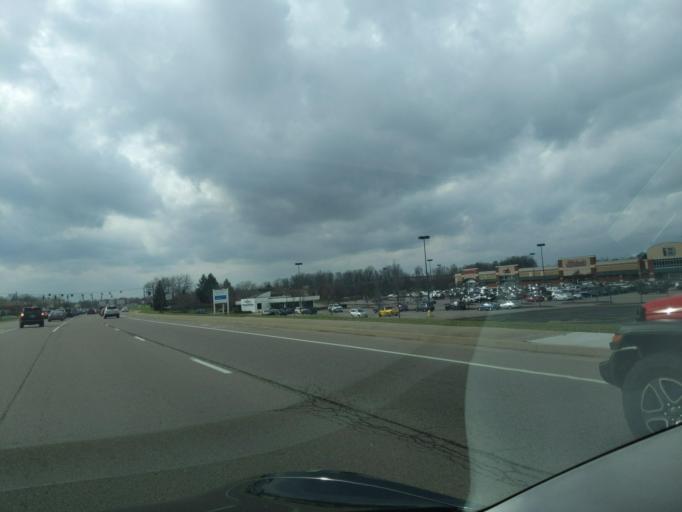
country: US
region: Kentucky
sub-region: Boone County
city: Florence
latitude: 39.0142
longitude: -84.6388
